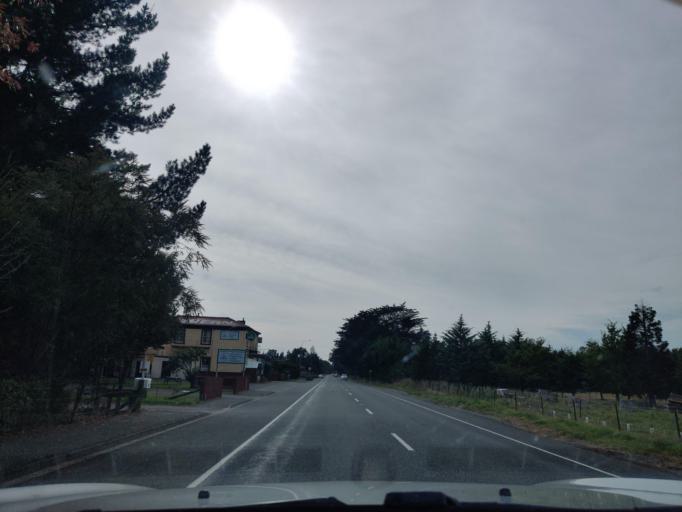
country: NZ
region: Nelson
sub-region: Nelson City
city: Nelson
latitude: -41.5642
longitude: 173.5319
